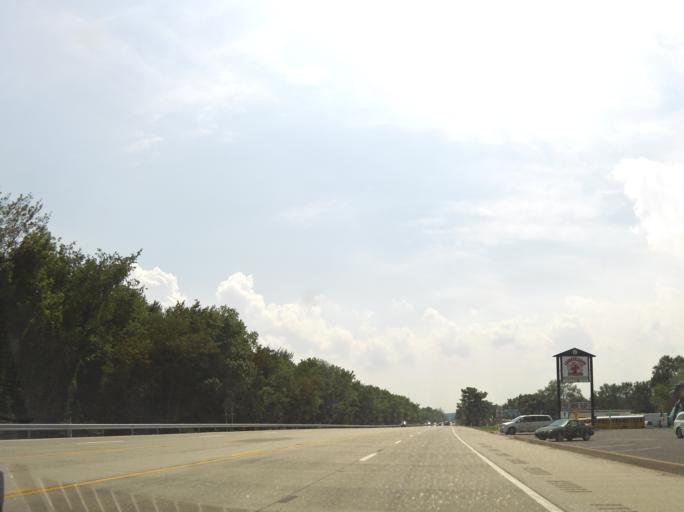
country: US
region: Pennsylvania
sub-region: Dauphin County
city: Matamoras
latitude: 40.4556
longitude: -76.9642
